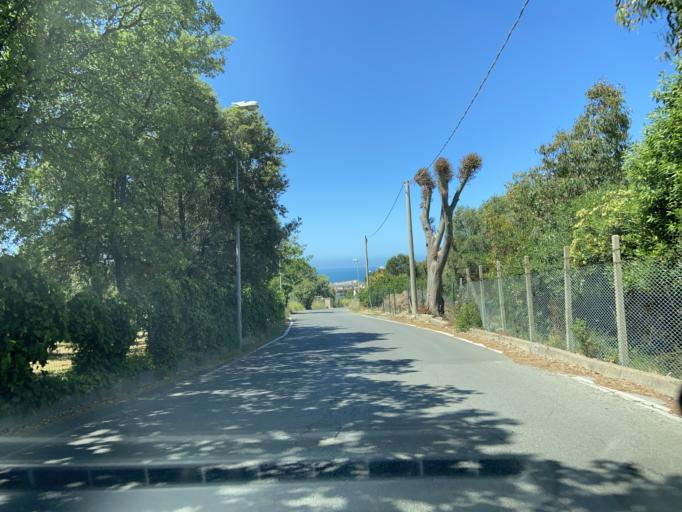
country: IT
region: Latium
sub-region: Citta metropolitana di Roma Capitale
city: Civitavecchia
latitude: 42.0855
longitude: 11.8206
